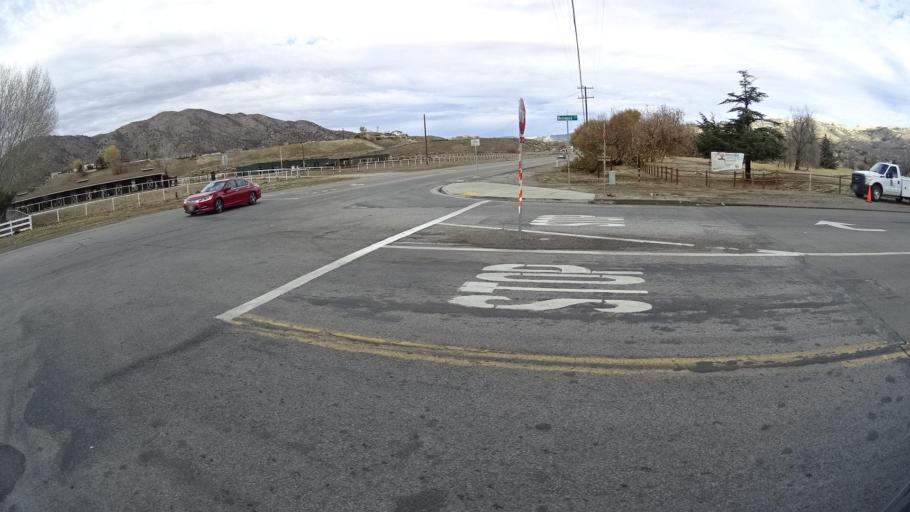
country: US
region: California
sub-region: Kern County
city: Golden Hills
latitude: 35.1441
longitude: -118.4946
